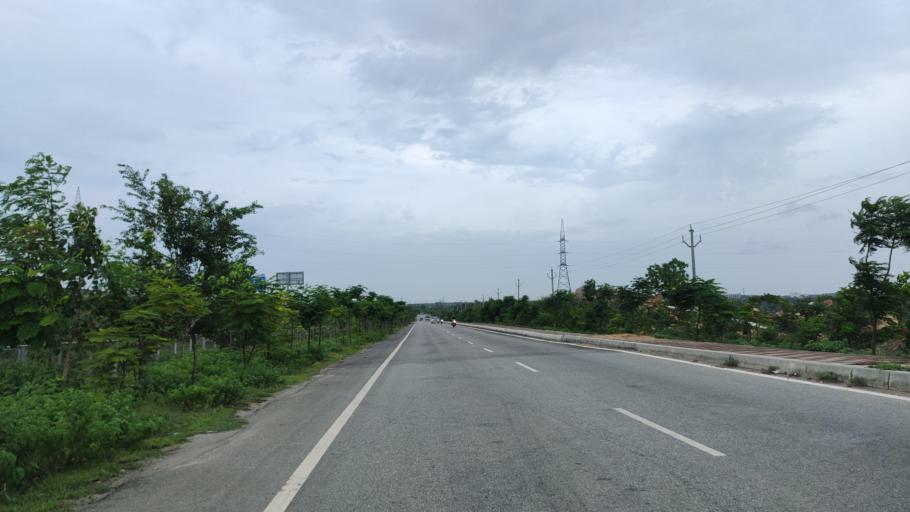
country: IN
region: Telangana
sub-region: Rangareddi
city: Secunderabad
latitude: 17.5790
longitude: 78.5837
